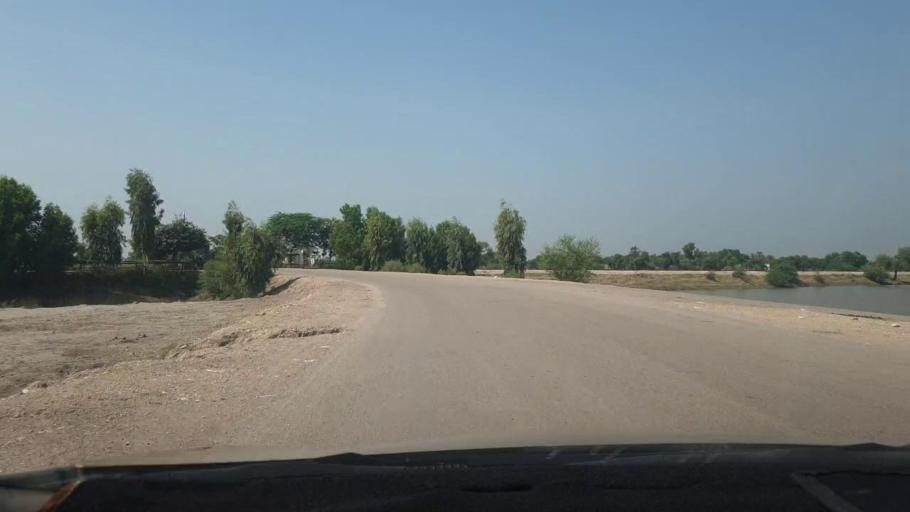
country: PK
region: Sindh
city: Larkana
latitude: 27.5975
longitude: 68.2436
